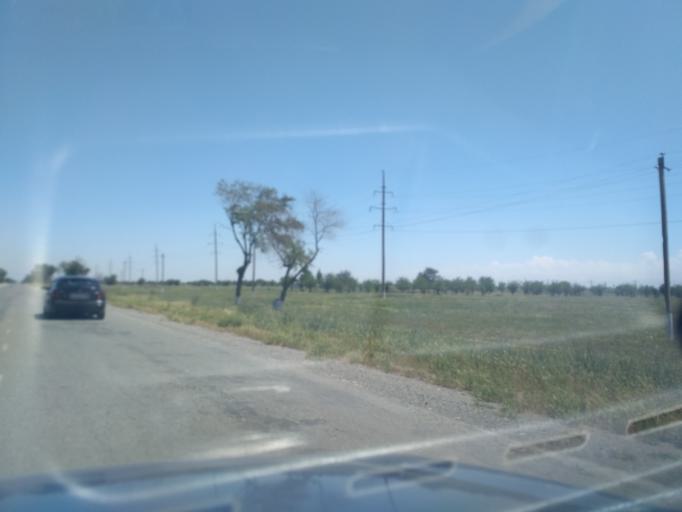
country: TJ
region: Viloyati Sughd
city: Zafarobod
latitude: 40.2178
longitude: 68.8939
